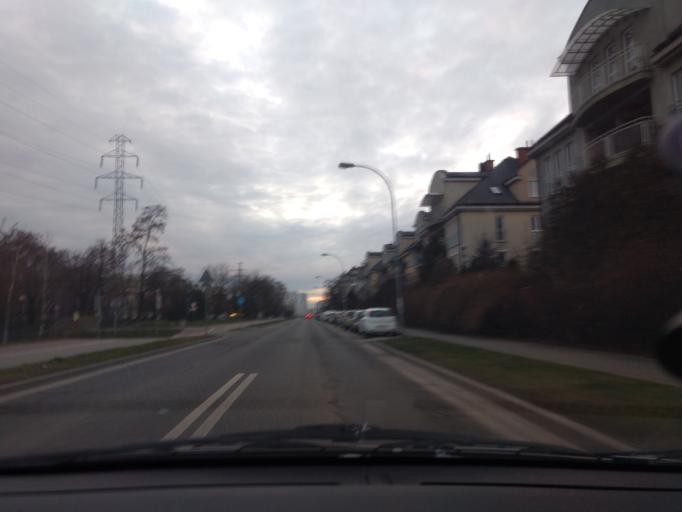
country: PL
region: Masovian Voivodeship
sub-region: Warszawa
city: Praga Poludnie
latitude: 52.2310
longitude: 21.0888
